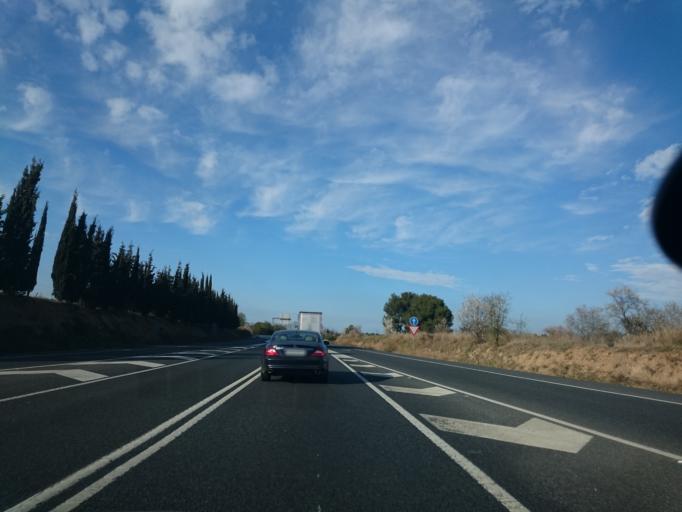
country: ES
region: Catalonia
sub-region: Provincia de Barcelona
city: Castellet
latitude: 41.3135
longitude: 1.6405
